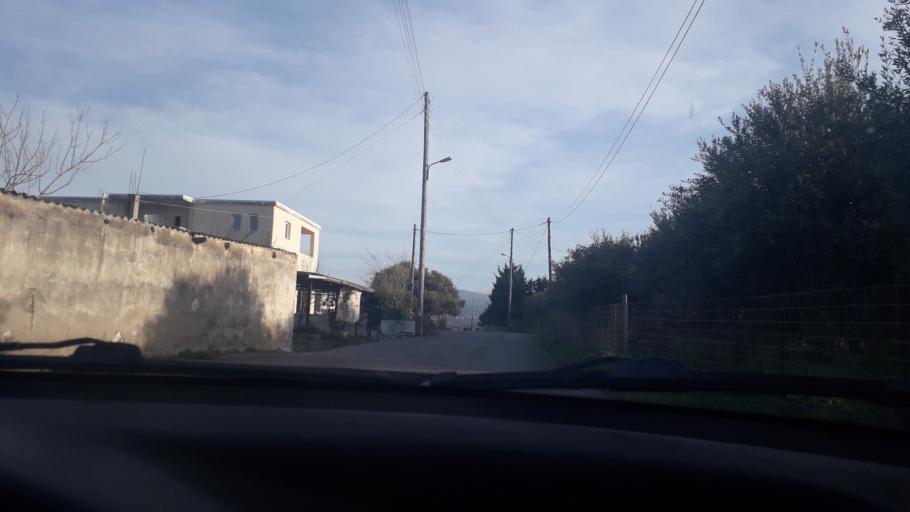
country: GR
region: Crete
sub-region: Nomos Rethymnis
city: Panormos
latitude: 35.3852
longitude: 24.6182
